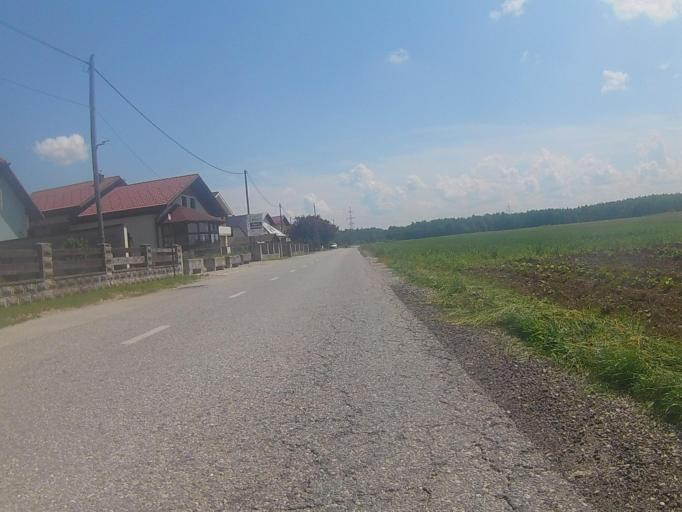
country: SI
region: Starse
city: Starse
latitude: 46.4437
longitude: 15.7675
